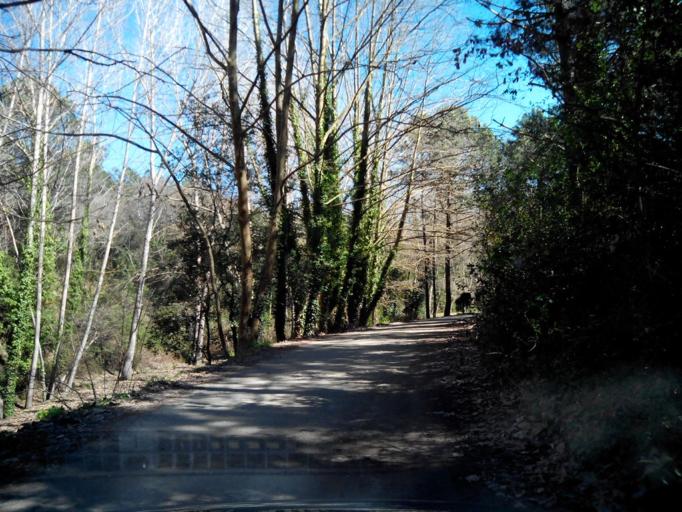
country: ES
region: Catalonia
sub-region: Provincia de Barcelona
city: Dosrius
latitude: 41.6039
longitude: 2.4534
